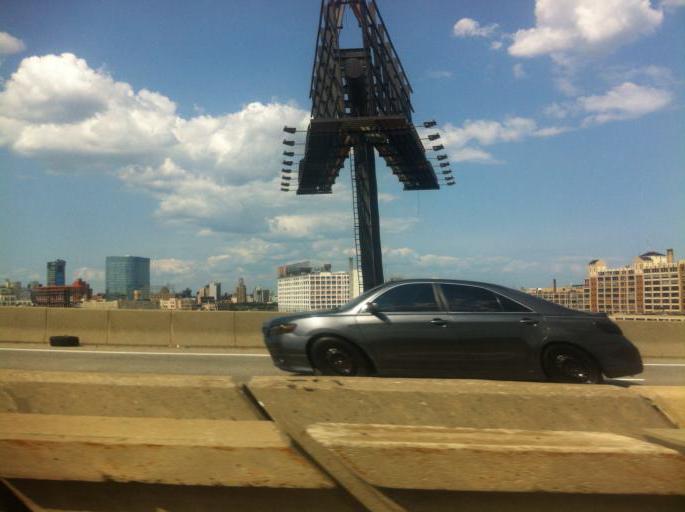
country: US
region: New York
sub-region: Queens County
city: Long Island City
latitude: 40.7393
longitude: -73.9415
